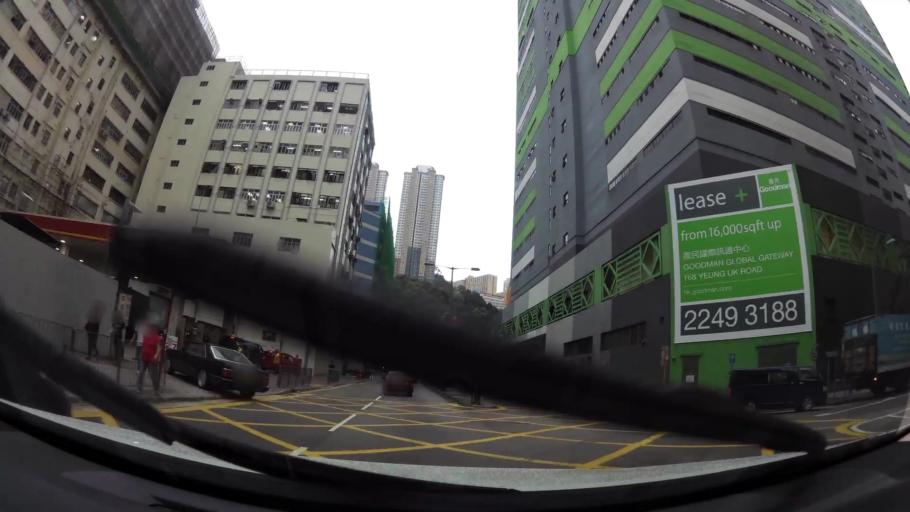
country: HK
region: Tsuen Wan
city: Tsuen Wan
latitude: 22.3664
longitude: 114.1190
